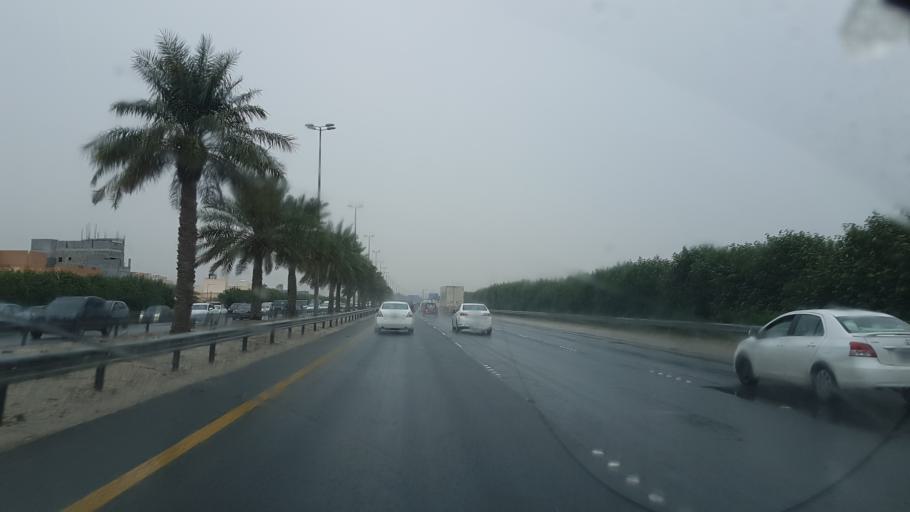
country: BH
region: Central Governorate
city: Madinat Hamad
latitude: 26.1564
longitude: 50.5061
